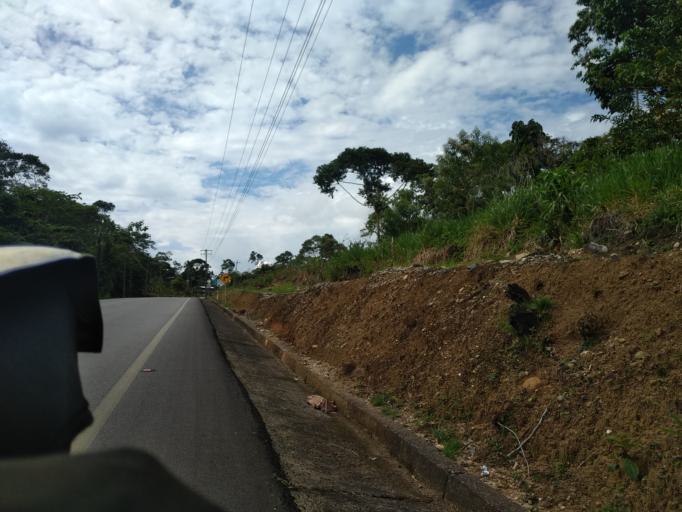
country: EC
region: Napo
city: Tena
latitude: -1.1189
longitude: -77.8103
